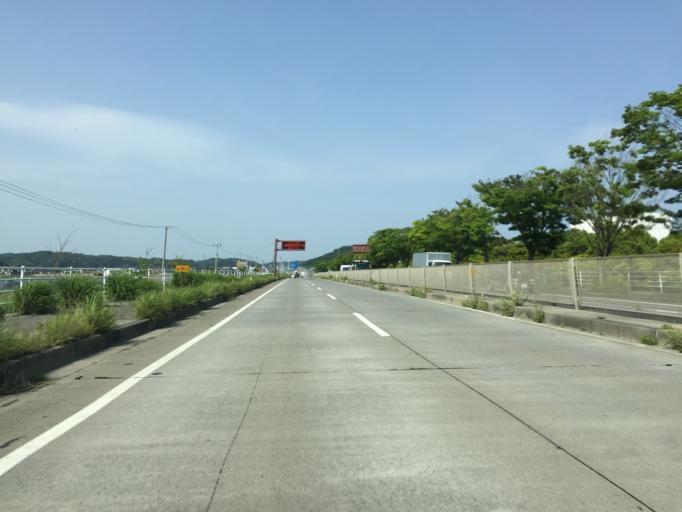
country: JP
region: Fukushima
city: Iwaki
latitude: 36.9665
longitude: 140.8839
